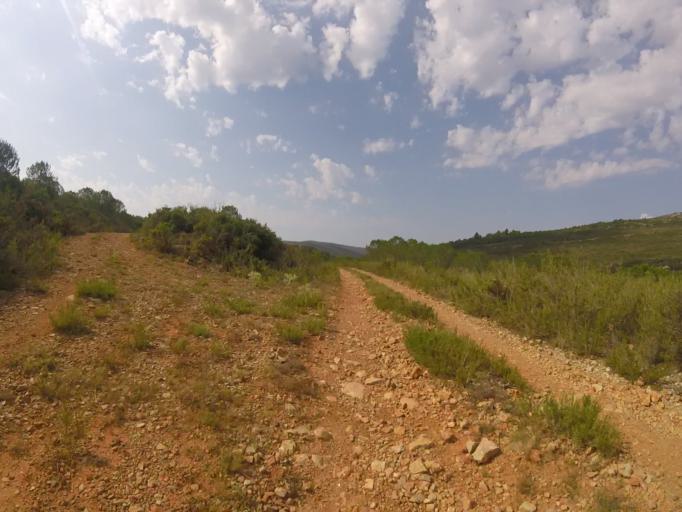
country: ES
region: Valencia
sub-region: Provincia de Castello
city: Alcala de Xivert
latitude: 40.3479
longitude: 0.1983
